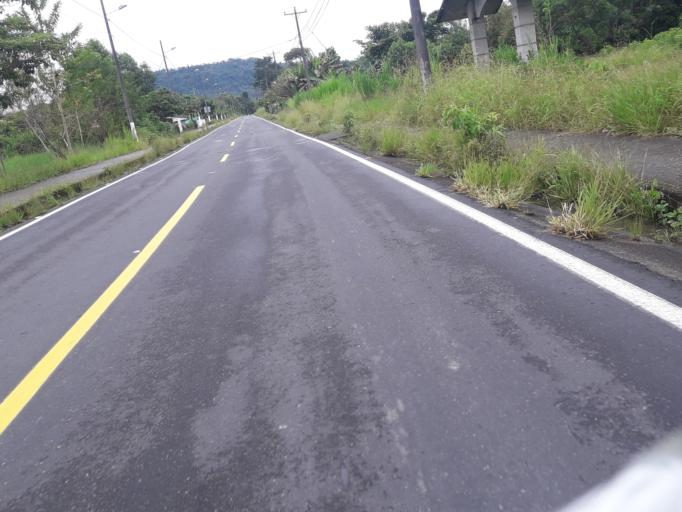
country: EC
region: Napo
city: Tena
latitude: -0.9717
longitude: -77.8554
